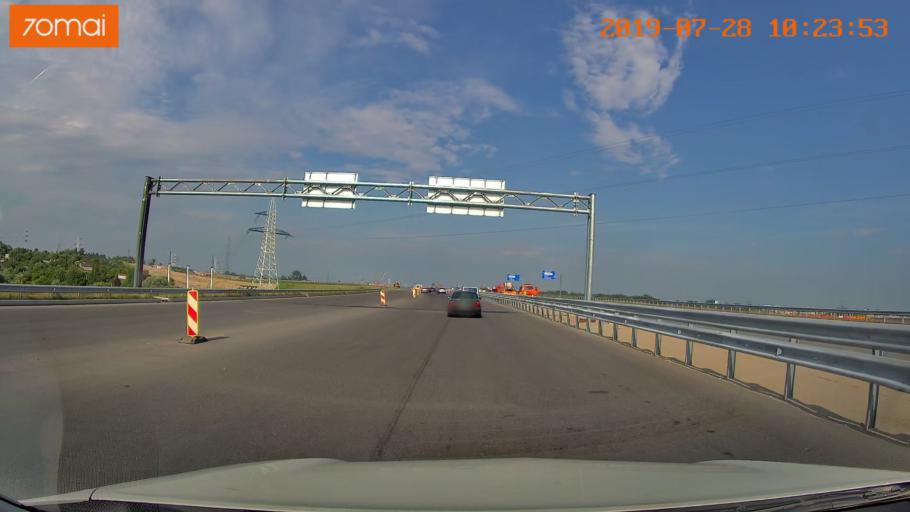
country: RU
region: Kaliningrad
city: Maloye Isakovo
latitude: 54.7677
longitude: 20.5550
